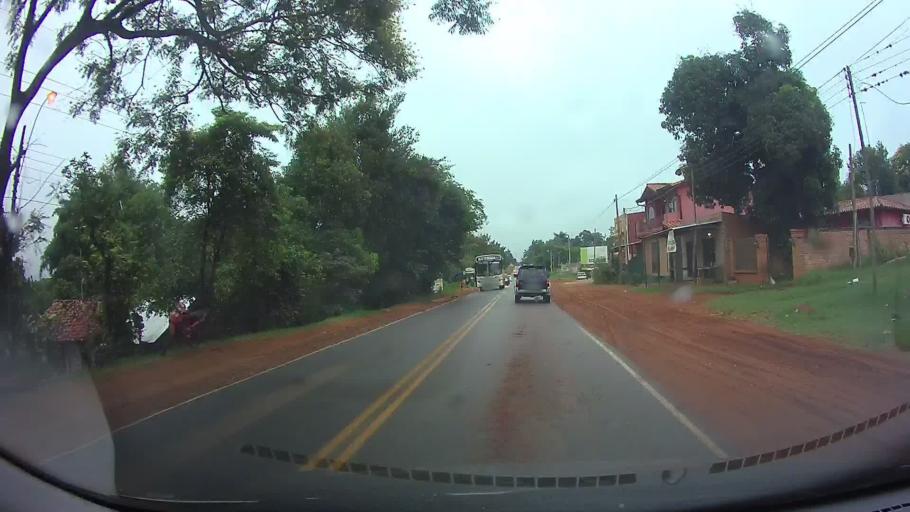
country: PY
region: Central
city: Itaugua
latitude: -25.4286
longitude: -57.3650
